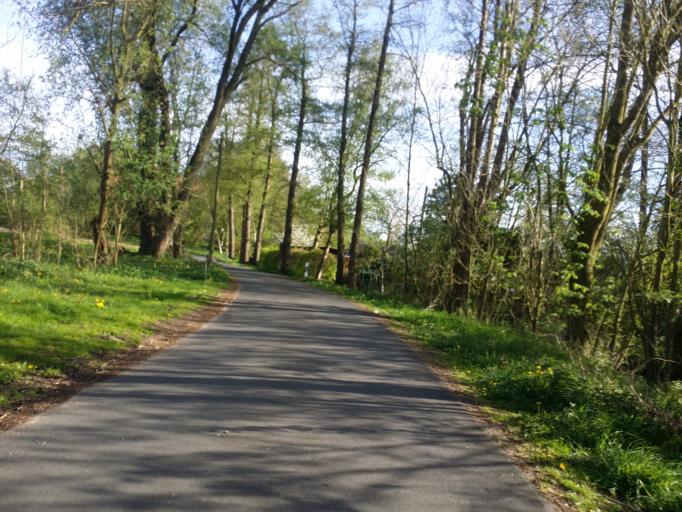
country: DE
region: Lower Saxony
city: Ritterhude
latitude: 53.1577
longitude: 8.7796
